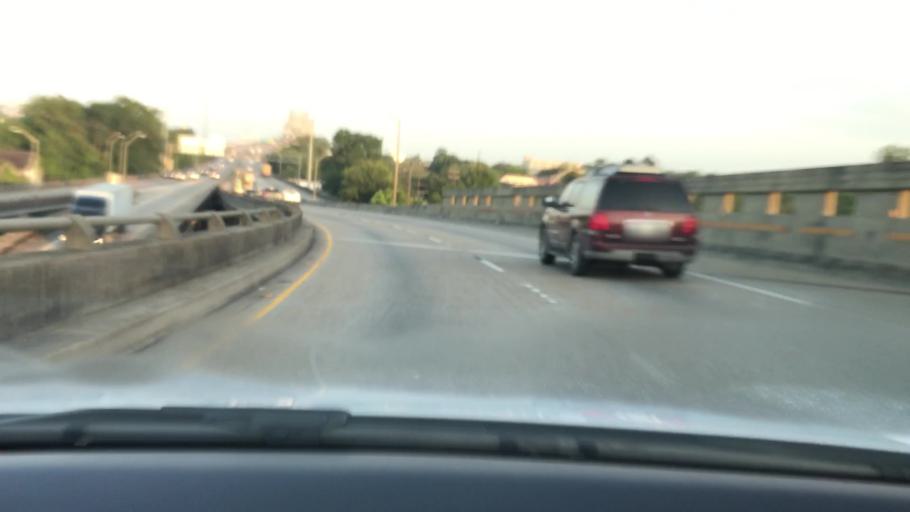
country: US
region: Louisiana
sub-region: East Baton Rouge Parish
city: Baton Rouge
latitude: 30.4393
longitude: -91.1798
